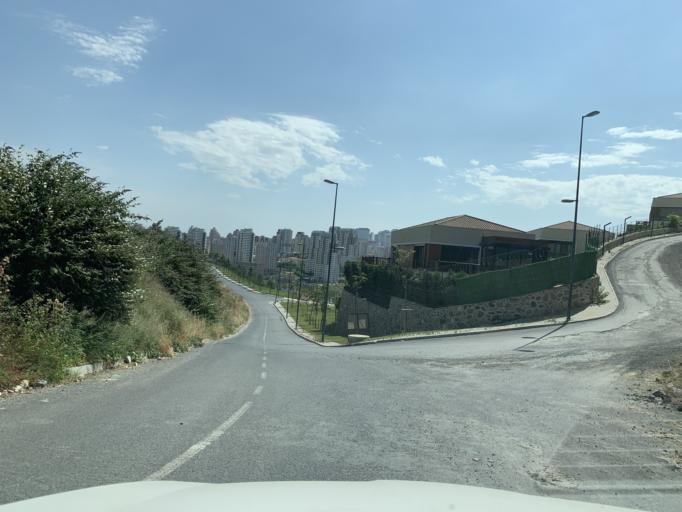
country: TR
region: Istanbul
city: Esenyurt
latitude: 41.0823
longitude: 28.6895
